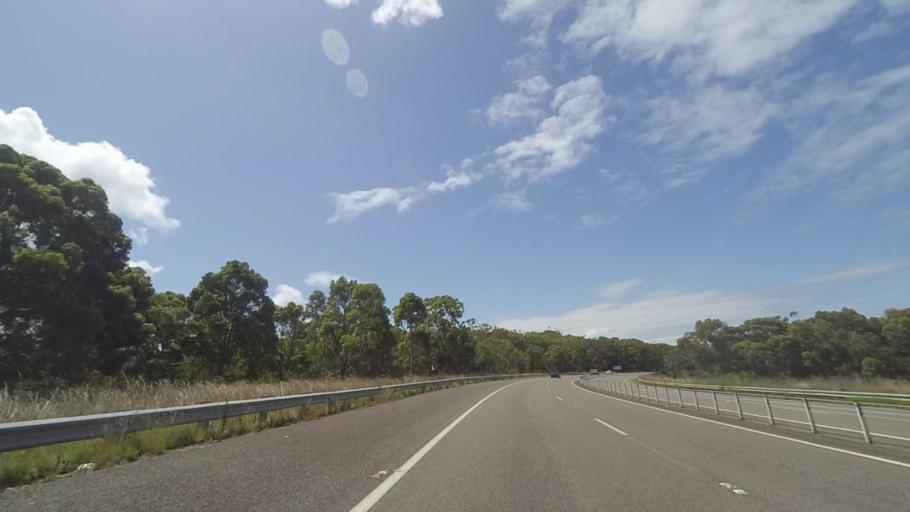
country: AU
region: New South Wales
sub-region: Wyong Shire
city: Kingfisher Shores
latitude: -33.1388
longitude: 151.6092
